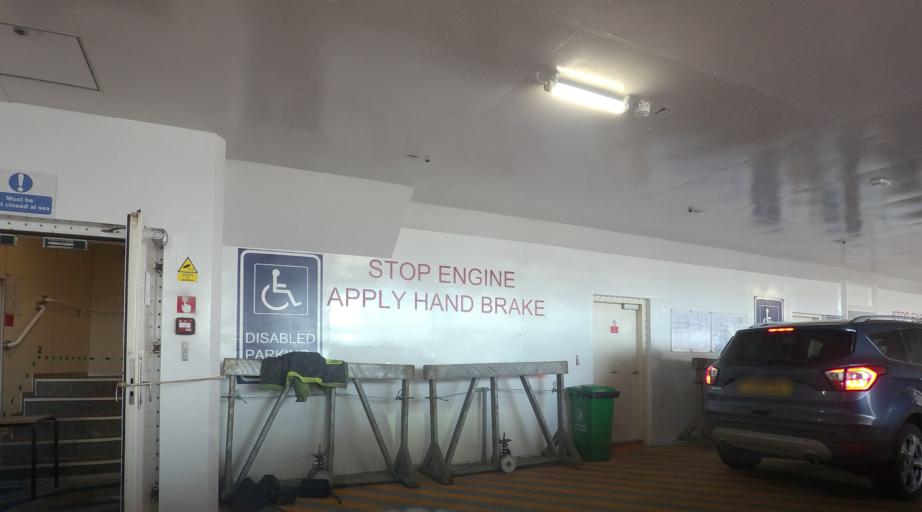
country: GB
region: Scotland
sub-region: Highland
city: Wick
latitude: 58.6393
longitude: -3.1609
